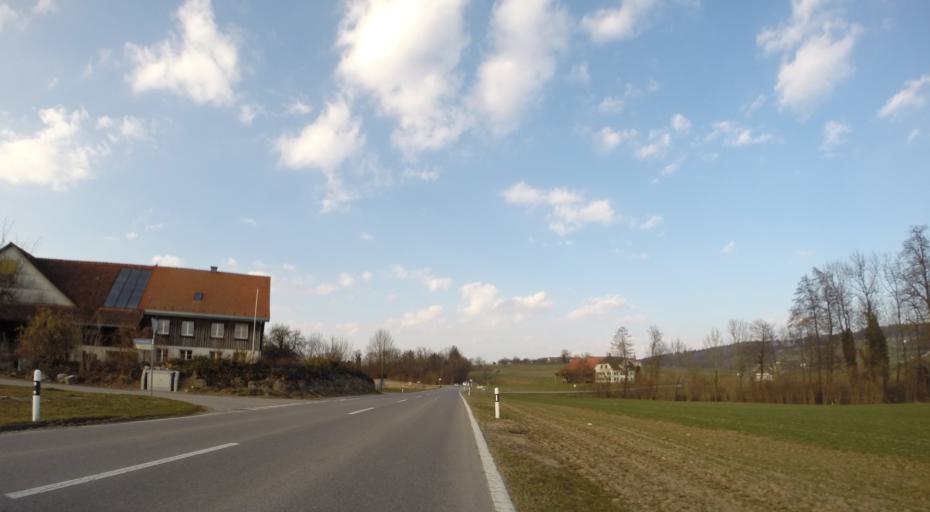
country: CH
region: Thurgau
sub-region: Frauenfeld District
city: Steckborn
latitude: 47.6439
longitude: 8.9780
